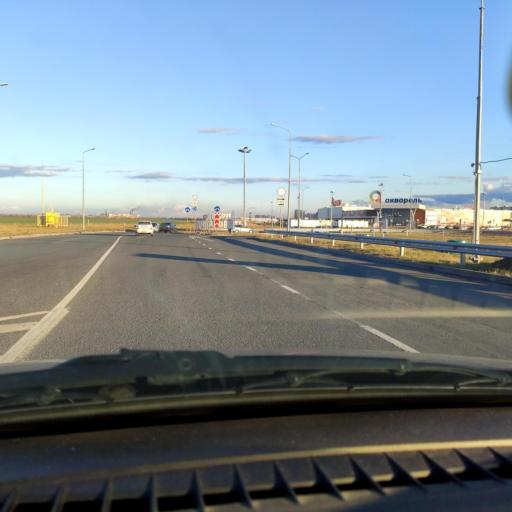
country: RU
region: Samara
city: Tol'yatti
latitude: 53.5528
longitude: 49.3412
